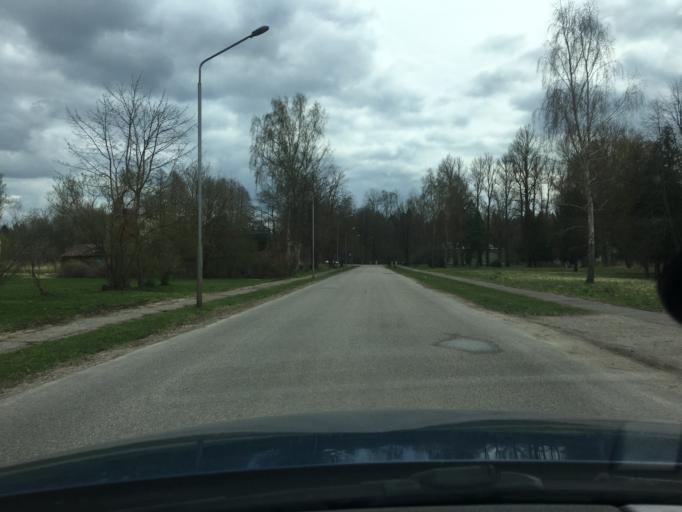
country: LV
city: Tireli
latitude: 56.9430
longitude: 23.4908
